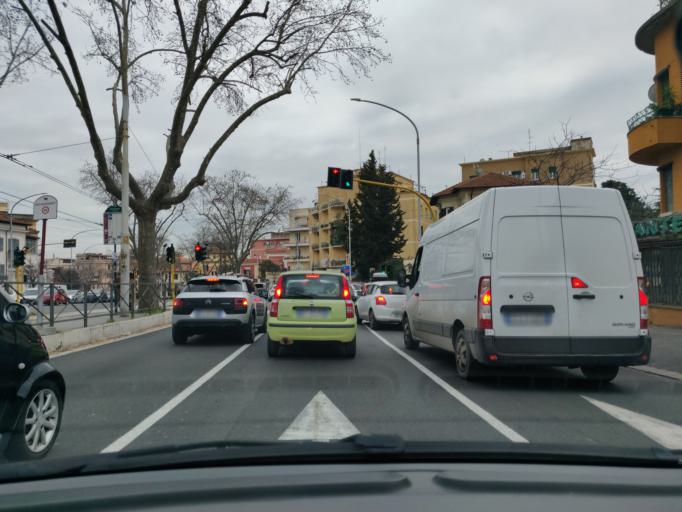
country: VA
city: Vatican City
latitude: 41.8716
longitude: 12.4498
